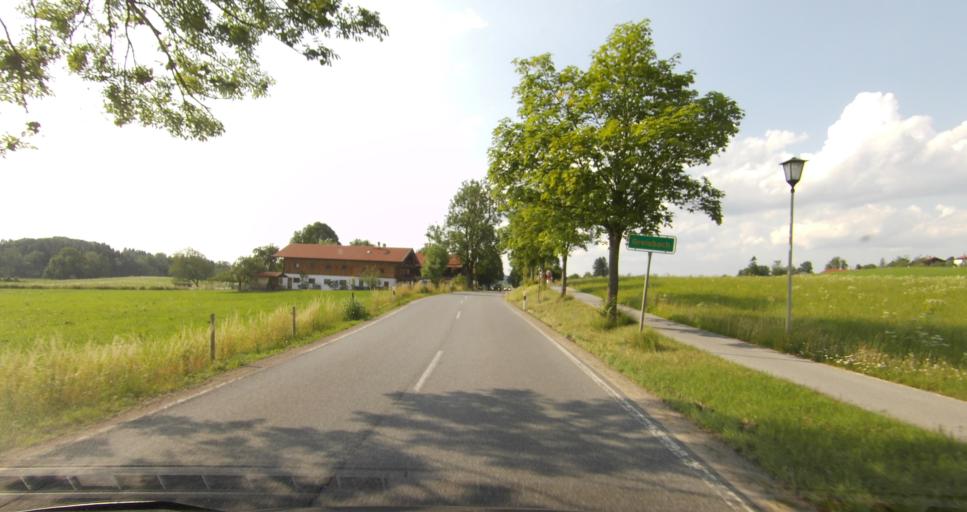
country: DE
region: Bavaria
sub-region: Upper Bavaria
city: Fischbachau
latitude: 47.7477
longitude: 11.9484
